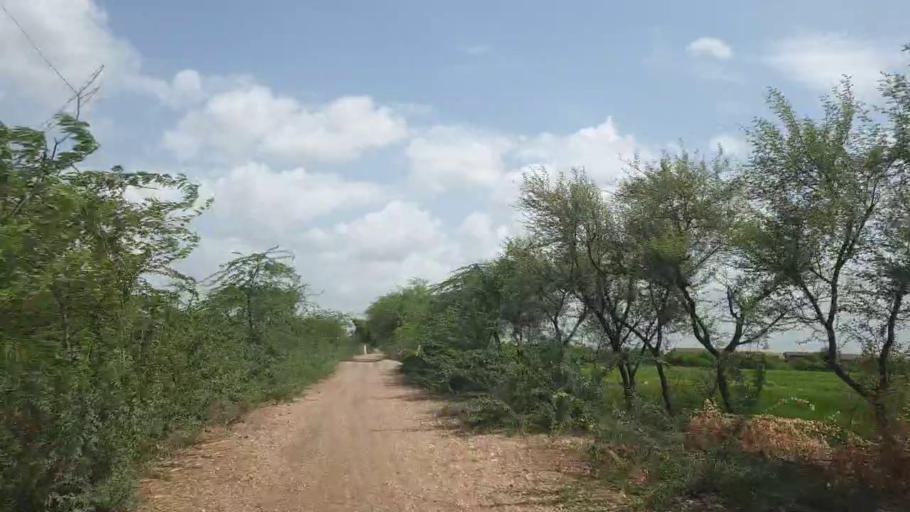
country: PK
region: Sindh
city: Tando Bago
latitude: 24.6513
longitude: 68.9930
